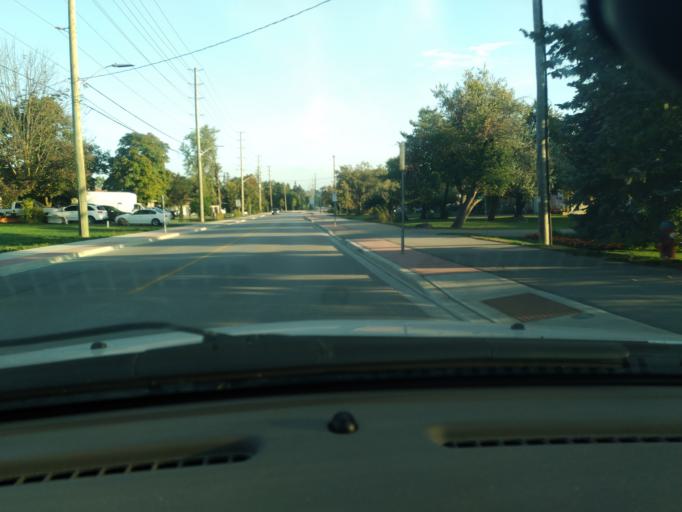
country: CA
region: Ontario
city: Bradford West Gwillimbury
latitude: 44.0923
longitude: -79.5671
